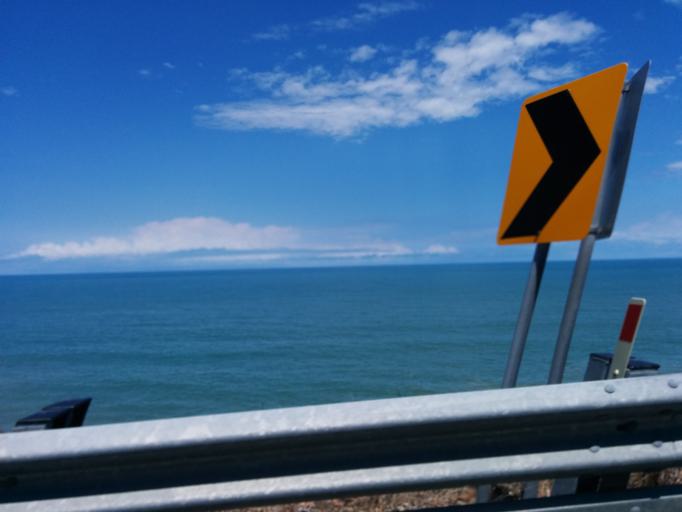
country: AU
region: Queensland
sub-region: Cairns
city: Port Douglas
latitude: -16.6180
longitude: 145.5405
